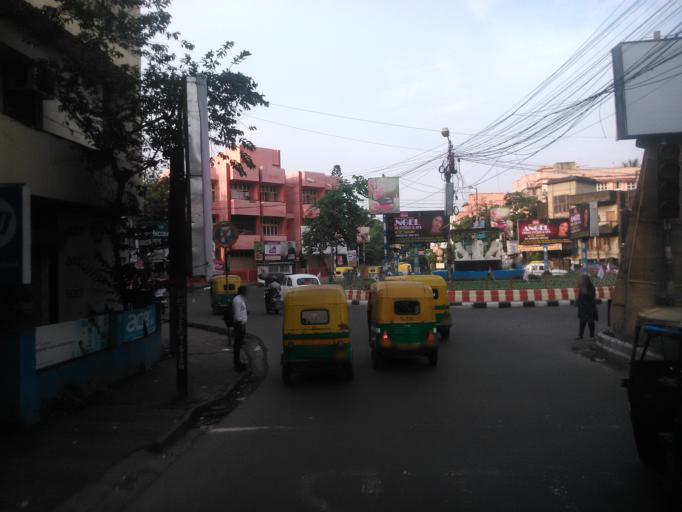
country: IN
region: West Bengal
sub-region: North 24 Parganas
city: Garui
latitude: 22.5914
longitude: 88.3993
